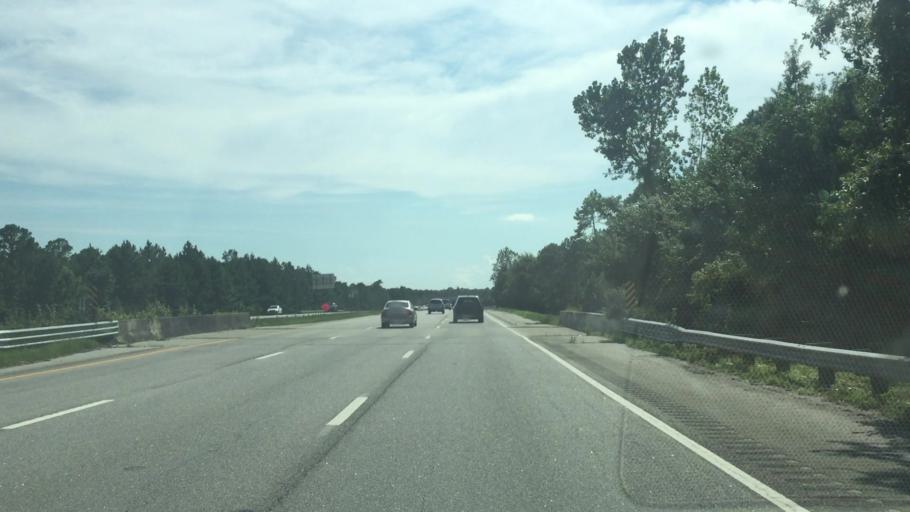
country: US
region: South Carolina
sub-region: Horry County
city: North Myrtle Beach
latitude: 33.8326
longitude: -78.7153
